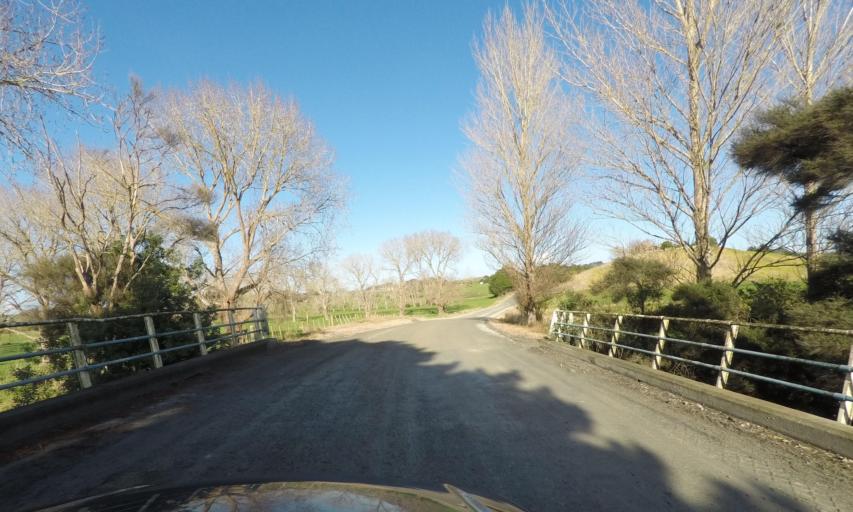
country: NZ
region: Auckland
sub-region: Auckland
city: Wellsford
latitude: -36.1509
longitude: 174.6064
